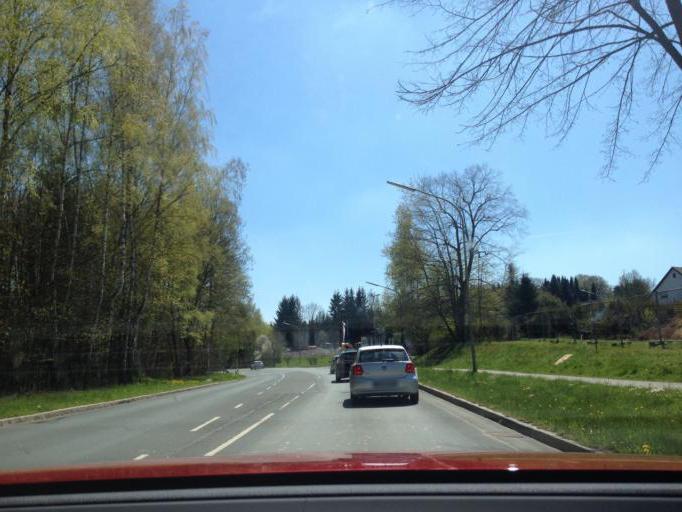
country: DE
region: Bavaria
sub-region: Upper Franconia
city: Oberkotzau
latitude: 50.2565
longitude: 11.9344
